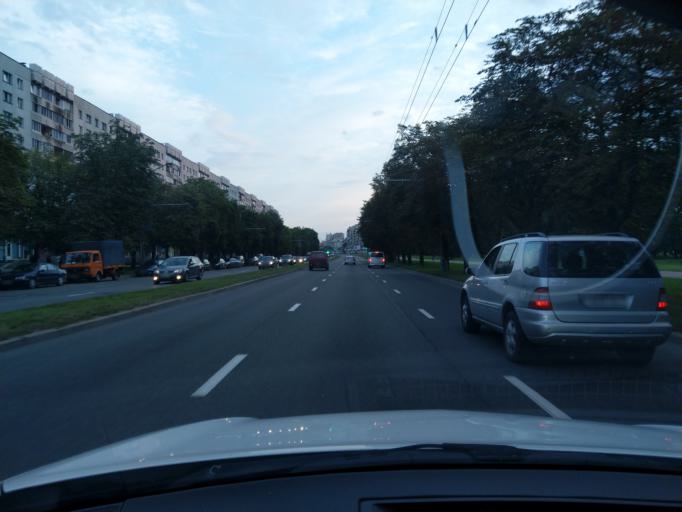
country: BY
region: Minsk
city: Minsk
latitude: 53.9297
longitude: 27.5750
